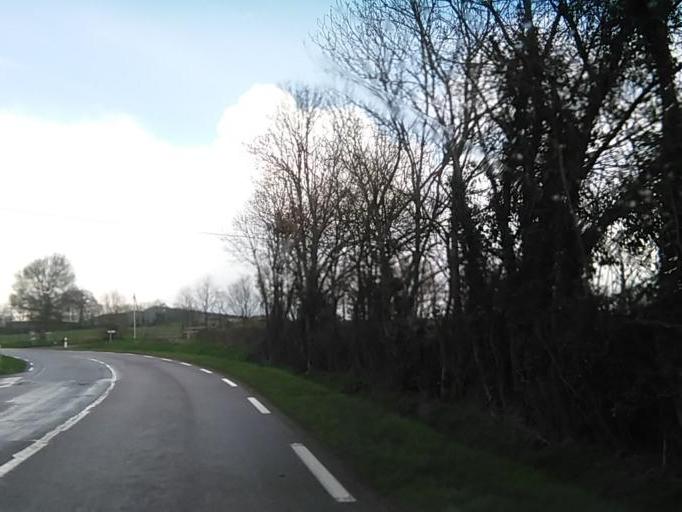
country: FR
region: Lower Normandy
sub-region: Departement de l'Orne
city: Pont-Ecrepin
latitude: 48.7742
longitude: -0.2497
